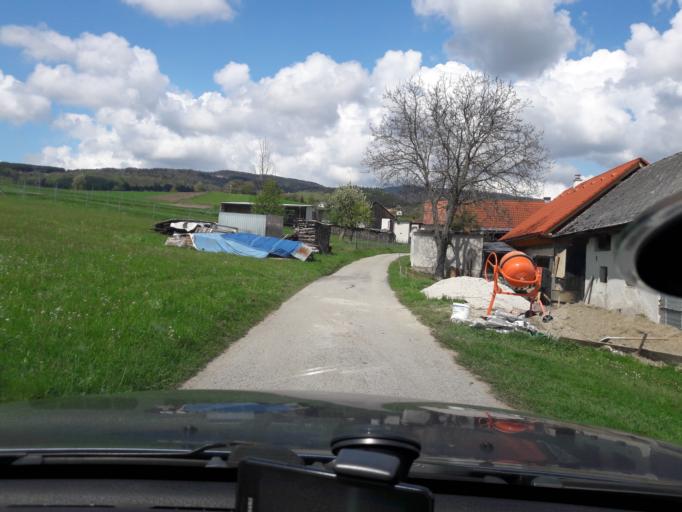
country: SK
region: Banskobystricky
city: Hrinova
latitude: 48.5833
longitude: 19.4719
